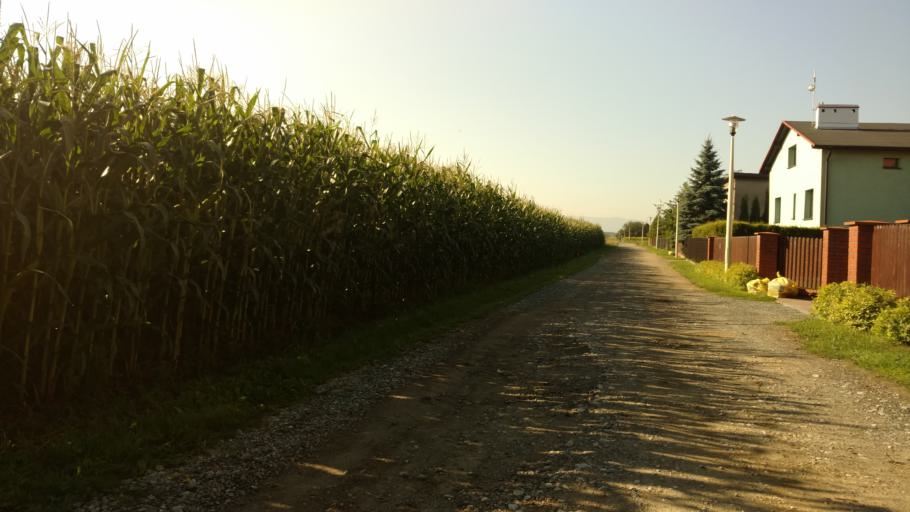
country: PL
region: Silesian Voivodeship
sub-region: Powiat pszczynski
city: Pszczyna
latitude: 49.9930
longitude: 18.9672
